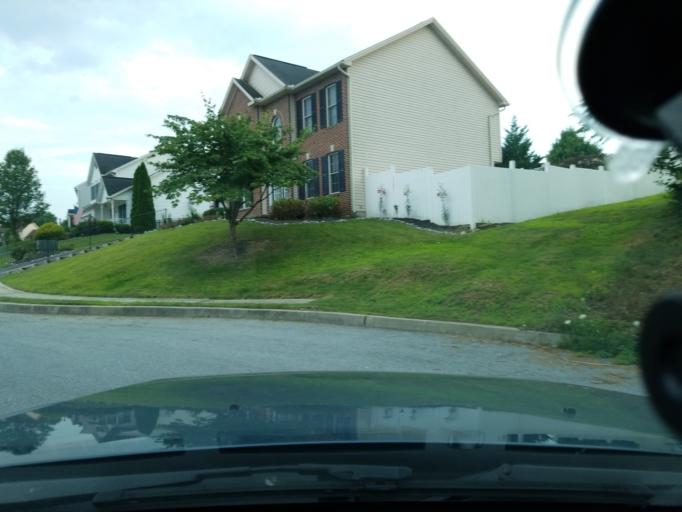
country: US
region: Pennsylvania
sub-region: Dauphin County
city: Hummelstown
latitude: 40.2723
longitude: -76.7272
